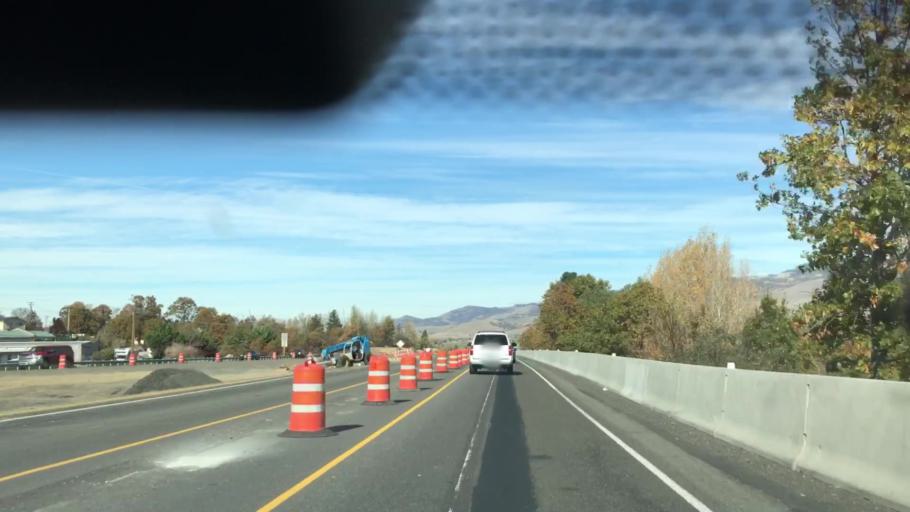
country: US
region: Oregon
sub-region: Jackson County
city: Ashland
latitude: 42.1750
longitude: -122.6590
